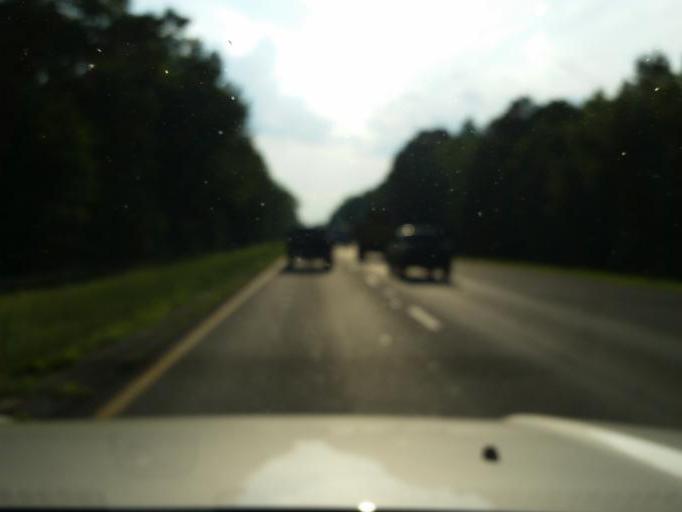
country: US
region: Virginia
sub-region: New Kent County
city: New Kent
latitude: 37.4966
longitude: -77.0295
